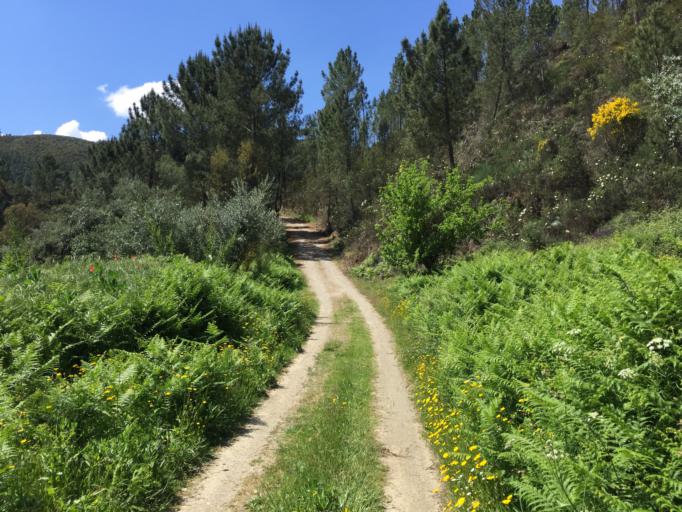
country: PT
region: Coimbra
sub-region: Pampilhosa da Serra
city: Pampilhosa da Serra
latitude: 40.0695
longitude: -7.7773
